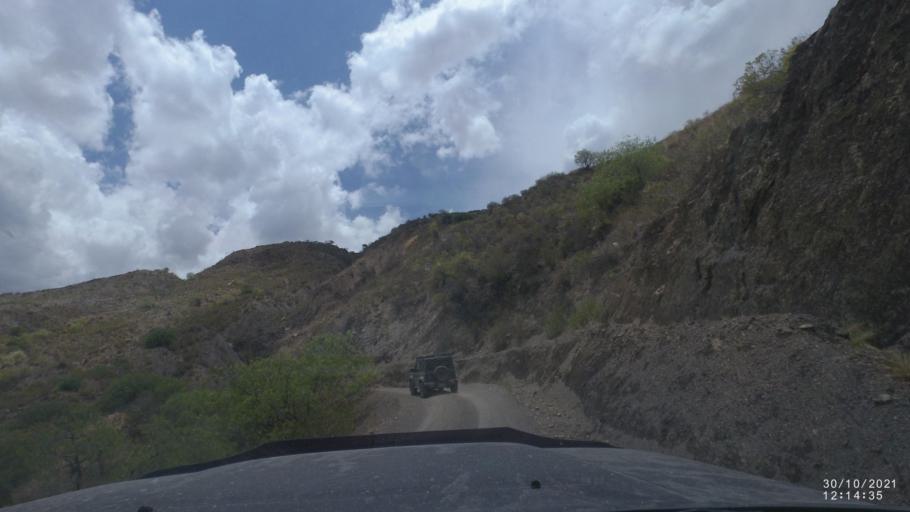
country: BO
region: Cochabamba
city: Colchani
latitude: -17.5597
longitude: -66.6236
